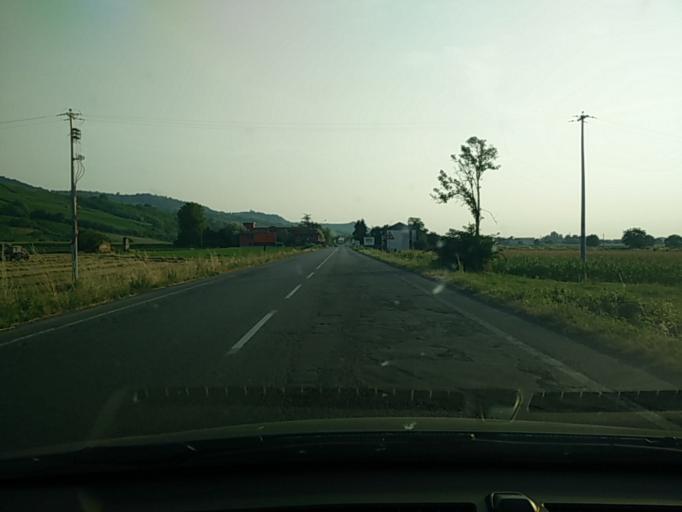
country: IT
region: Lombardy
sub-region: Provincia di Pavia
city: Redavalle
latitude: 45.0434
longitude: 9.2179
